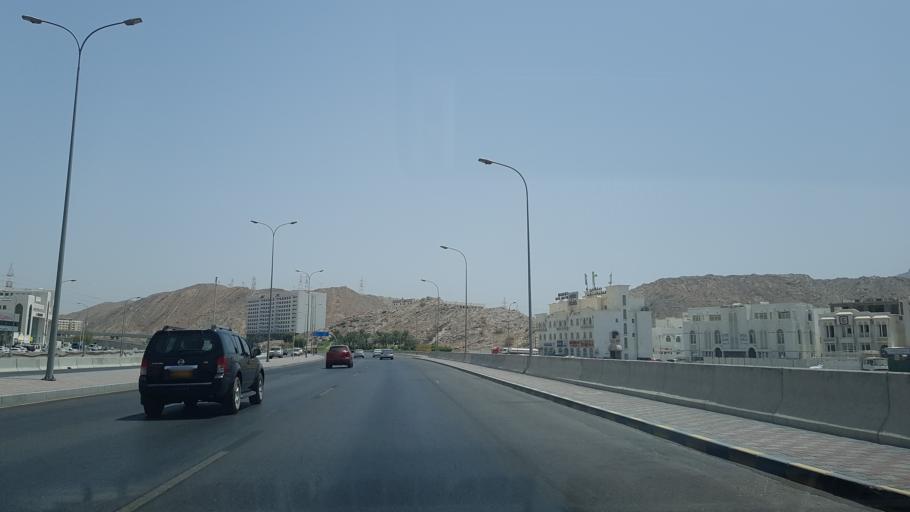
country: OM
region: Muhafazat Masqat
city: Muscat
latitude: 23.5968
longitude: 58.5204
